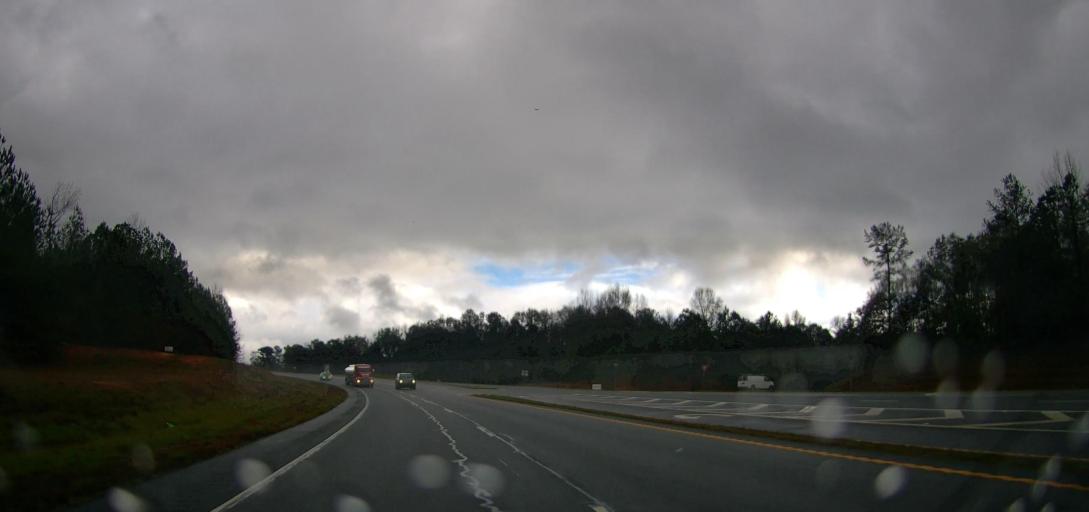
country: US
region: Georgia
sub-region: Jackson County
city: Nicholson
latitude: 34.0624
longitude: -83.4247
